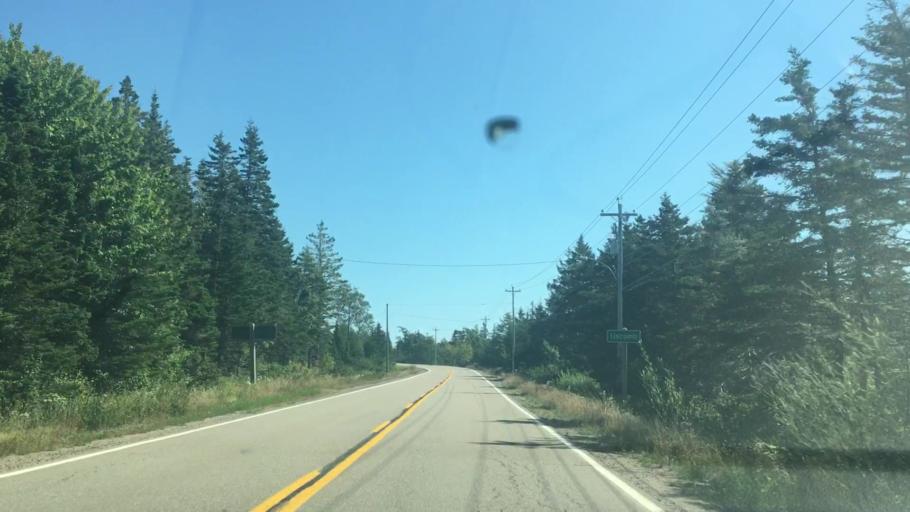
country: CA
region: Nova Scotia
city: Antigonish
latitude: 45.0217
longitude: -62.0095
